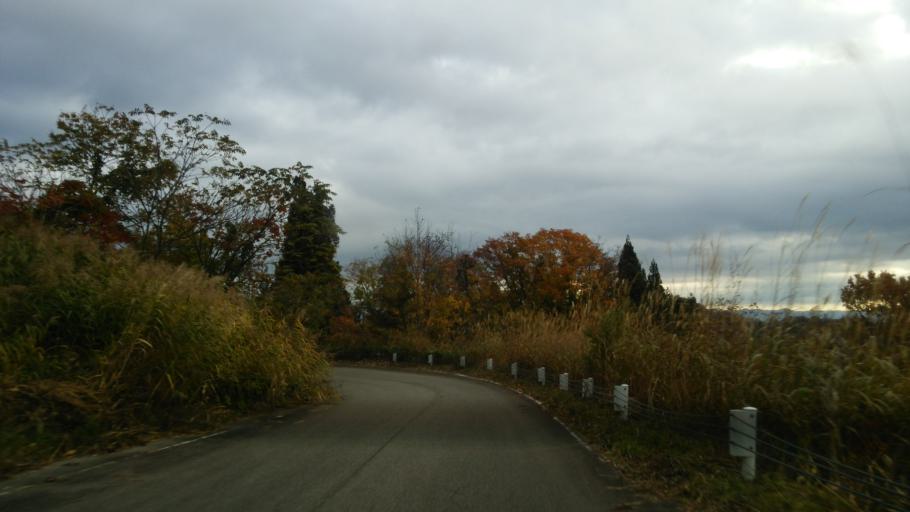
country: JP
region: Fukushima
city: Kitakata
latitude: 37.4052
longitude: 139.7649
